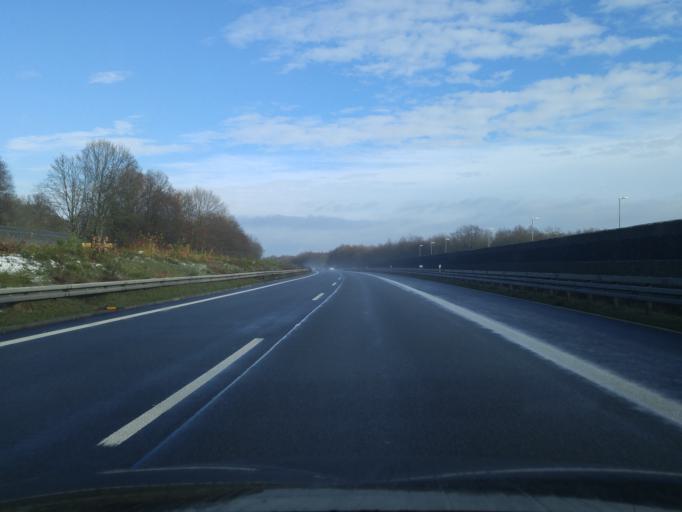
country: DE
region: Bavaria
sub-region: Regierungsbezirk Unterfranken
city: Arnstein
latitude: 49.9446
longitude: 10.0191
